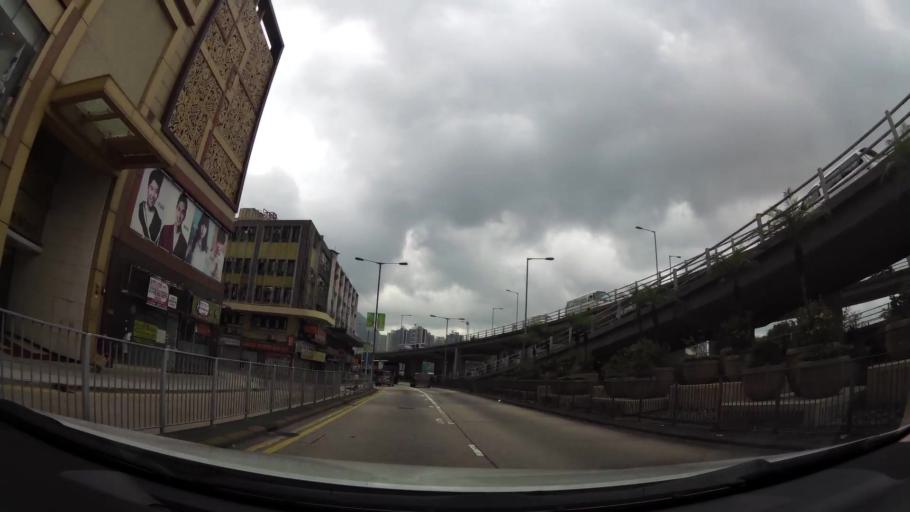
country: HK
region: Kowloon City
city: Kowloon
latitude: 22.3280
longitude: 114.1906
